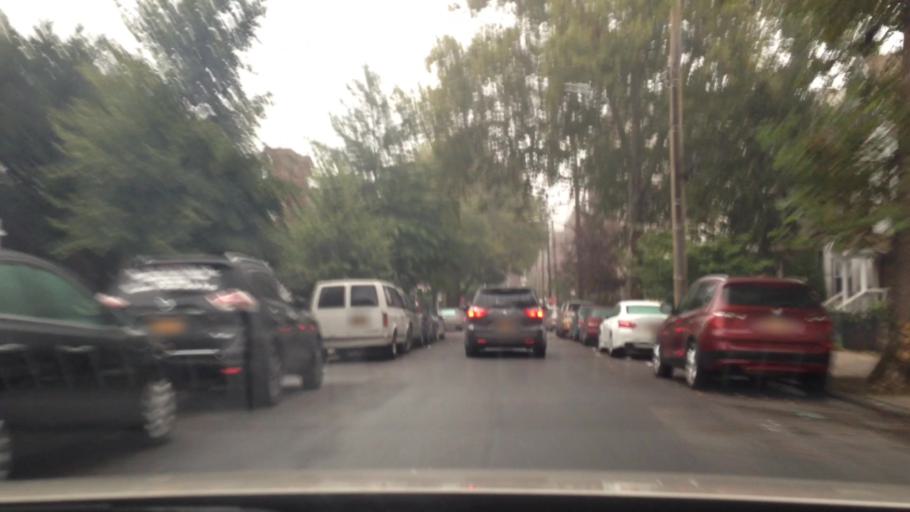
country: US
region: New York
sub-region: Kings County
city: East New York
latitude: 40.6786
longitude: -73.8919
